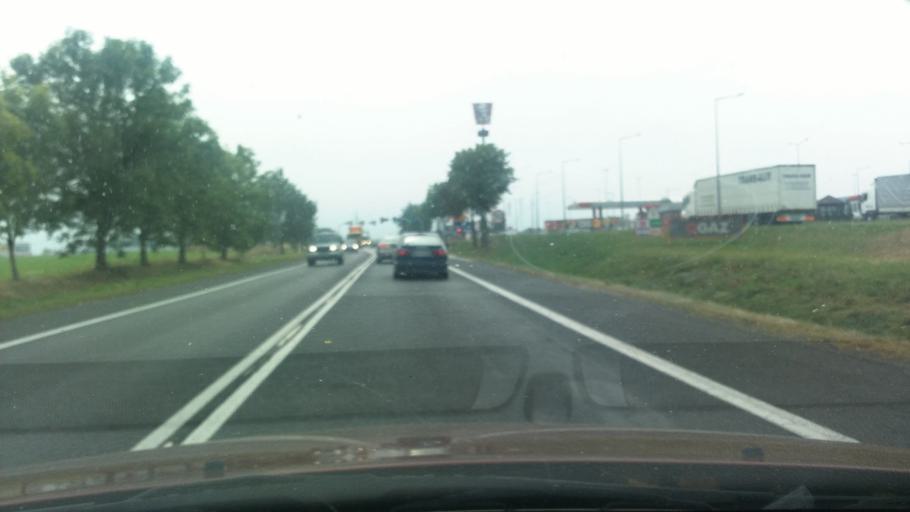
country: PL
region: Lower Silesian Voivodeship
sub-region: Powiat zgorzelecki
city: Lagow
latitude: 51.1617
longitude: 15.0294
